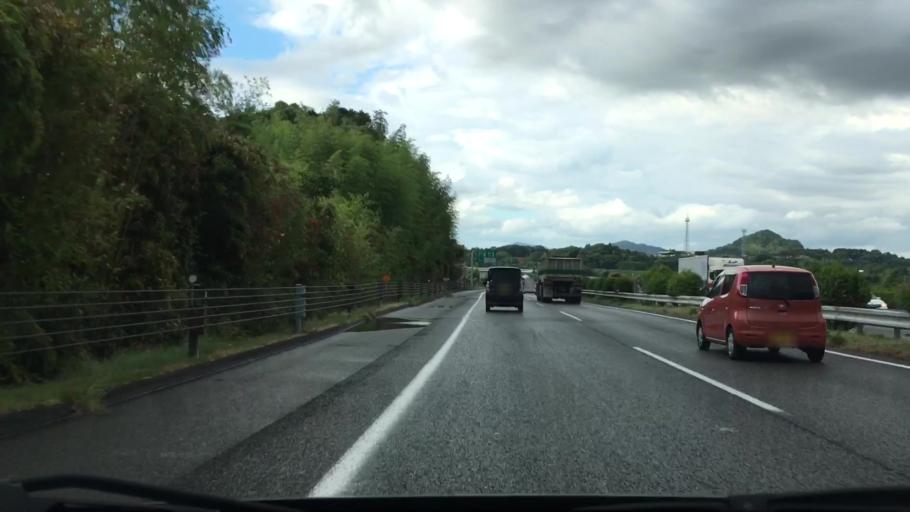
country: JP
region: Fukuoka
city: Koga
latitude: 33.7268
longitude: 130.5036
